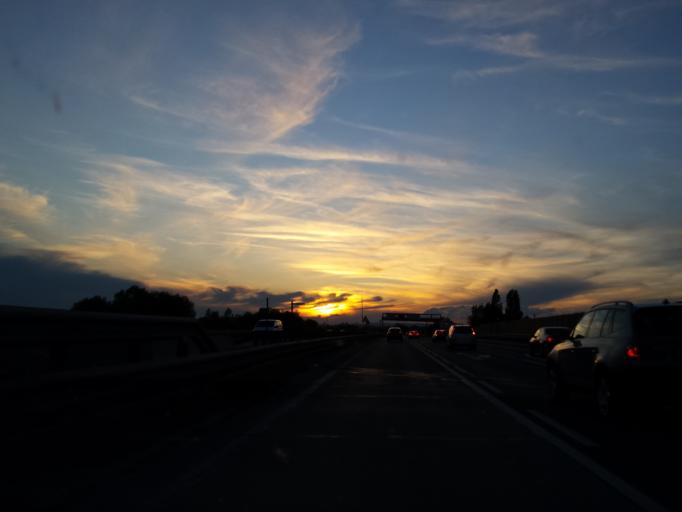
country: AT
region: Lower Austria
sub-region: Politischer Bezirk Wien-Umgebung
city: Schwechat
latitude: 48.1489
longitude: 16.4954
